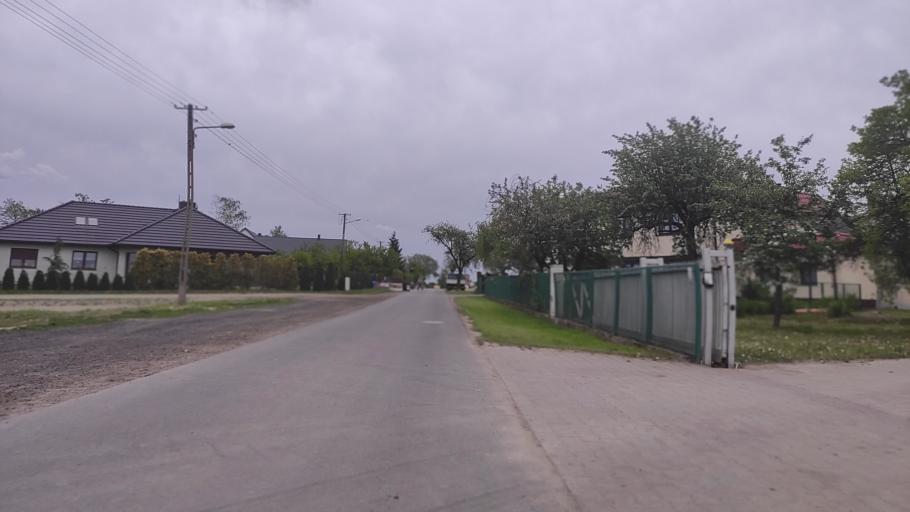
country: PL
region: Greater Poland Voivodeship
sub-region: Powiat poznanski
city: Swarzedz
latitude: 52.4100
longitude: 17.1309
